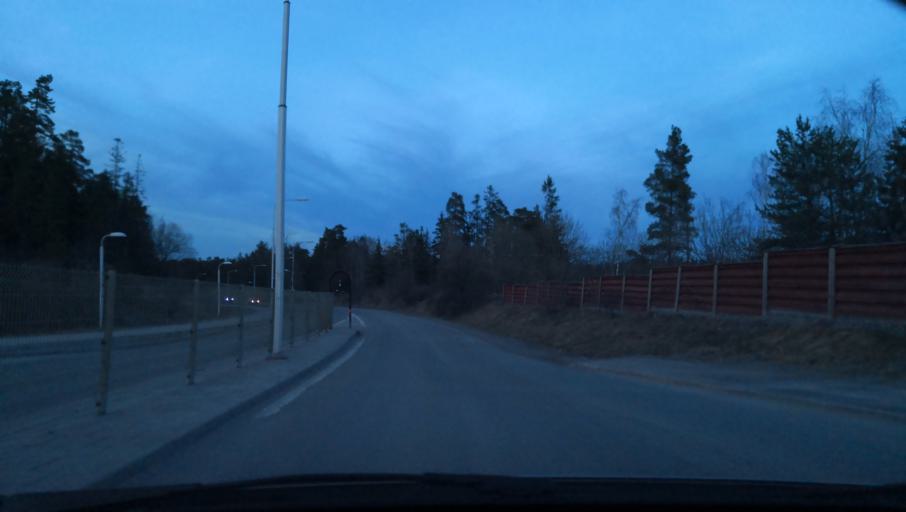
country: SE
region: Stockholm
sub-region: Varmdo Kommun
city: Gustavsberg
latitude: 59.3133
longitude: 18.3902
